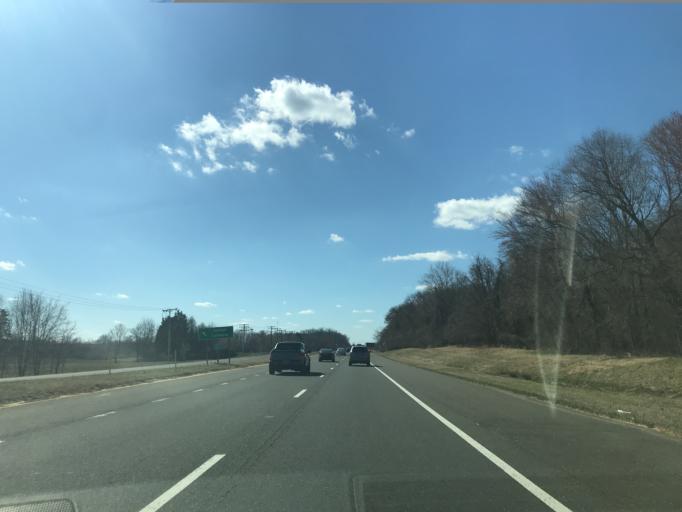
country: US
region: Maryland
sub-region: Prince George's County
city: Mitchellville
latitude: 38.9016
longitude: -76.7632
